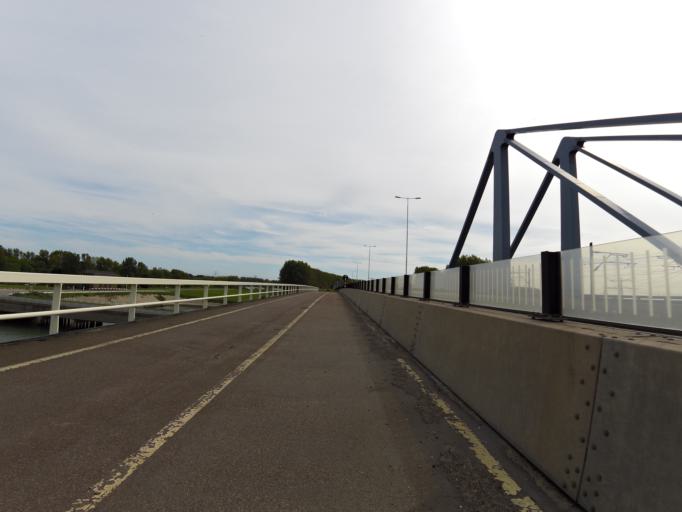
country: NL
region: South Holland
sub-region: Gemeente Rotterdam
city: Hoek van Holland
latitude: 51.9373
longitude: 4.1068
